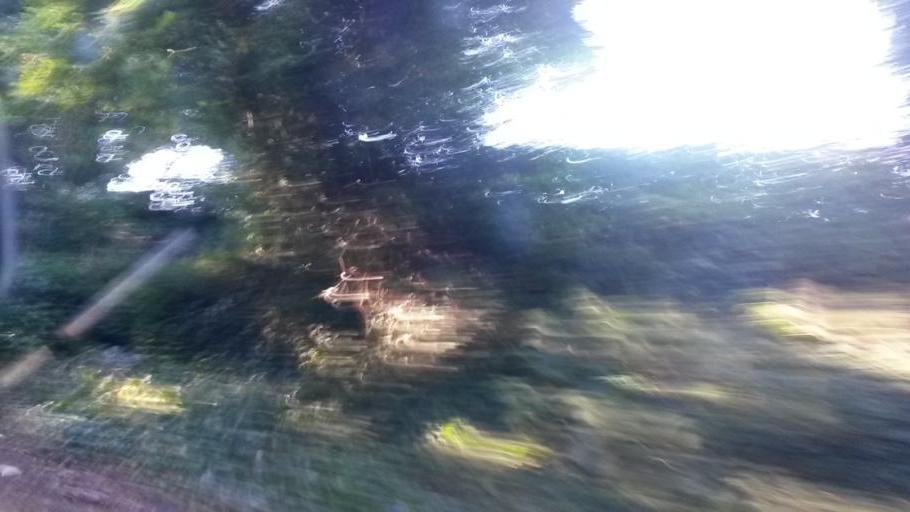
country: IE
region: Leinster
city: Ballymun
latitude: 53.4550
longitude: -6.2950
